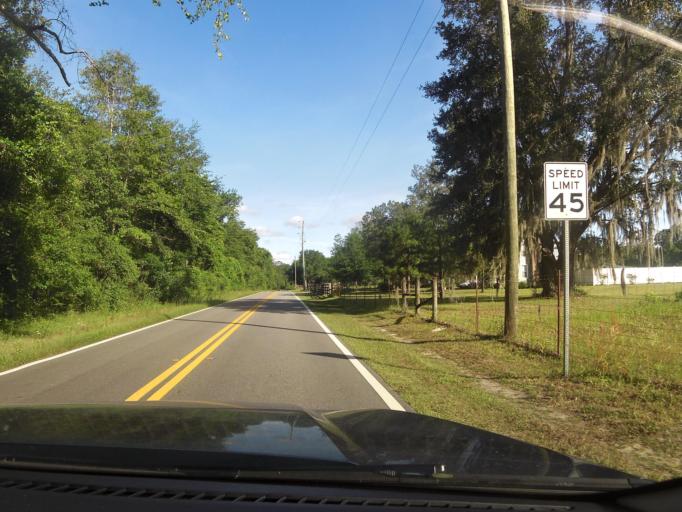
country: US
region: Florida
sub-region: Nassau County
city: Nassau Village-Ratliff
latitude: 30.4822
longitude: -81.8467
